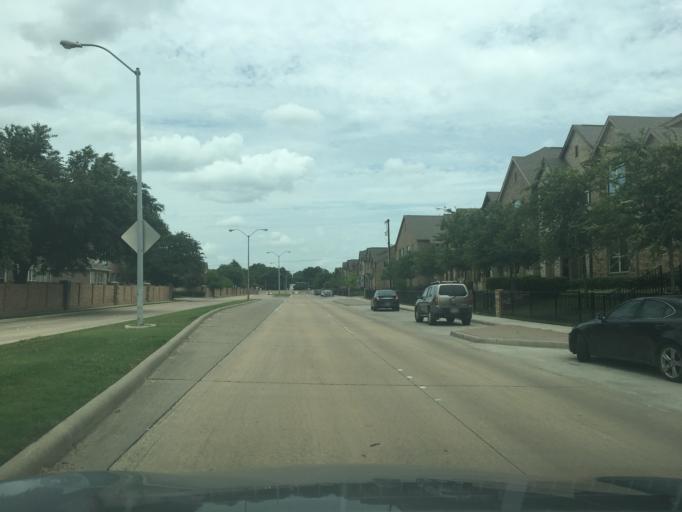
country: US
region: Texas
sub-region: Dallas County
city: Richardson
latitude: 32.9356
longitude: -96.7256
